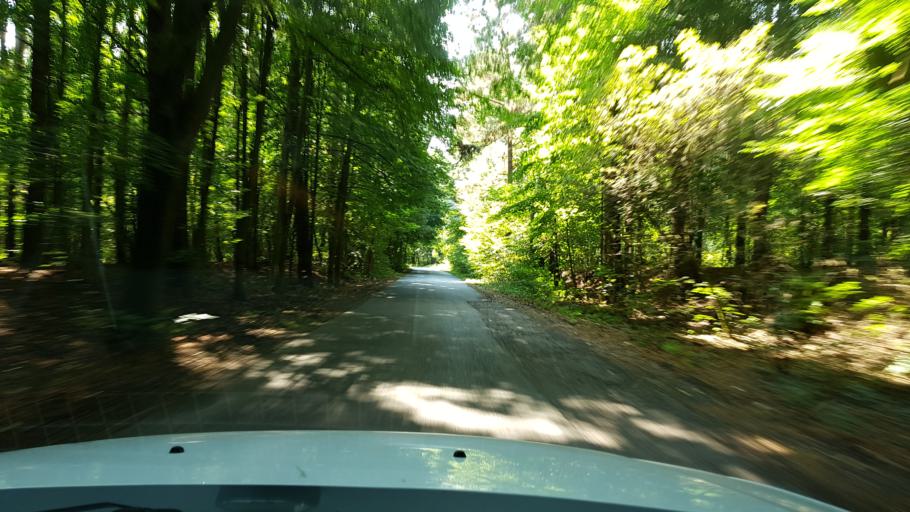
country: PL
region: West Pomeranian Voivodeship
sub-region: Powiat gryfinski
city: Chojna
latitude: 52.9416
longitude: 14.5137
